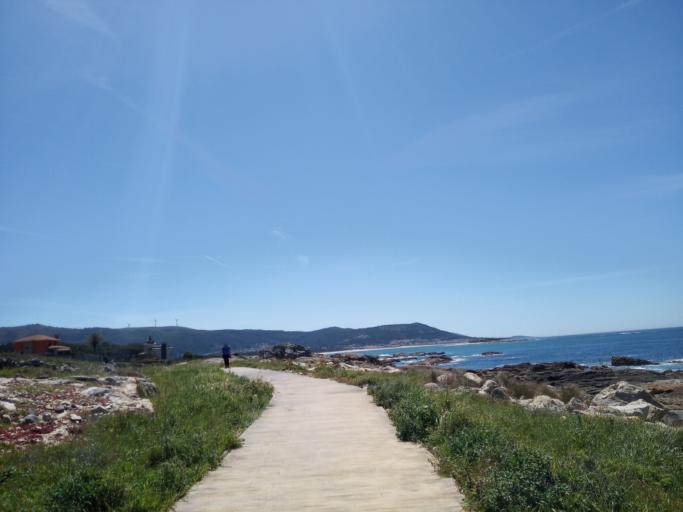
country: ES
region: Galicia
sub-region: Provincia de Pontevedra
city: A Guarda
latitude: 41.8752
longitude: -8.8763
